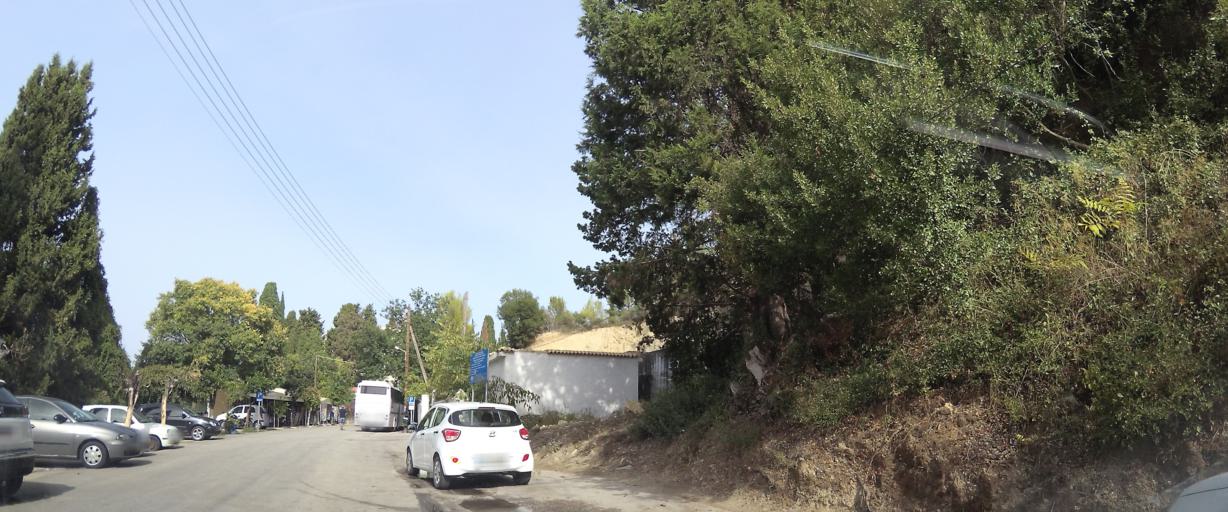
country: GR
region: Ionian Islands
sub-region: Nomos Kerkyras
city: Kynopiastes
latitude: 39.5614
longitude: 19.9031
